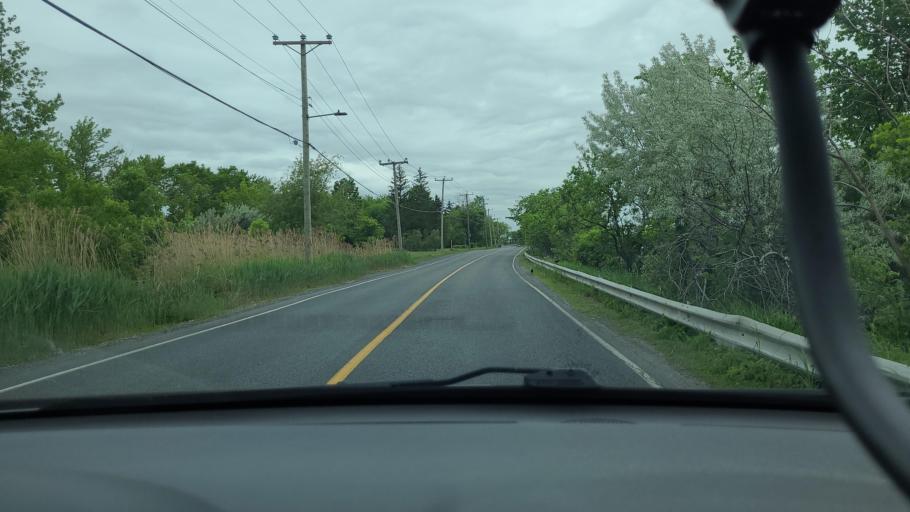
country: CA
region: Quebec
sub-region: Lanaudiere
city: Charlemagne
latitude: 45.6976
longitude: -73.5136
